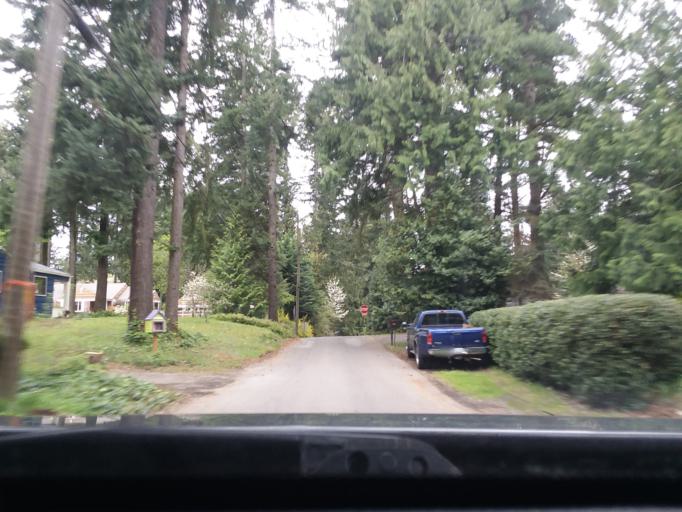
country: US
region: Washington
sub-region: King County
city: Shoreline
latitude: 47.7373
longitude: -122.3480
